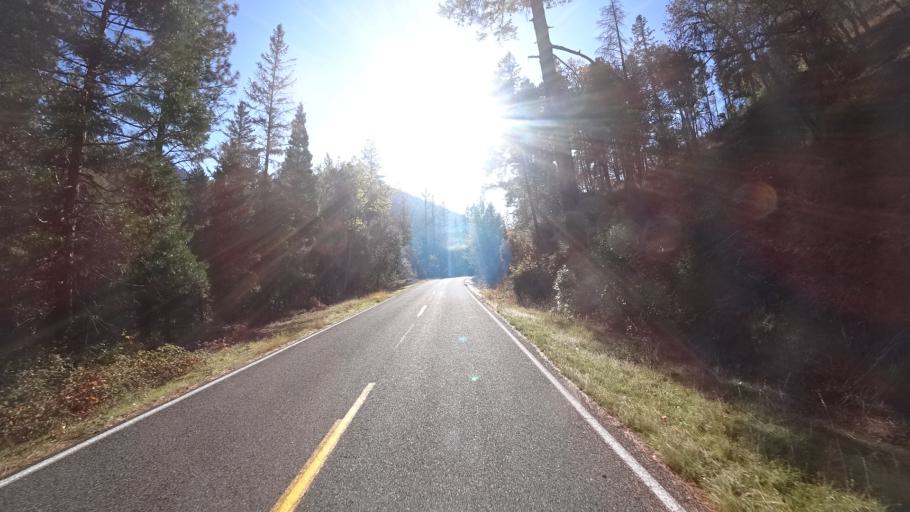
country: US
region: California
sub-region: Siskiyou County
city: Yreka
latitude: 41.8934
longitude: -122.8243
